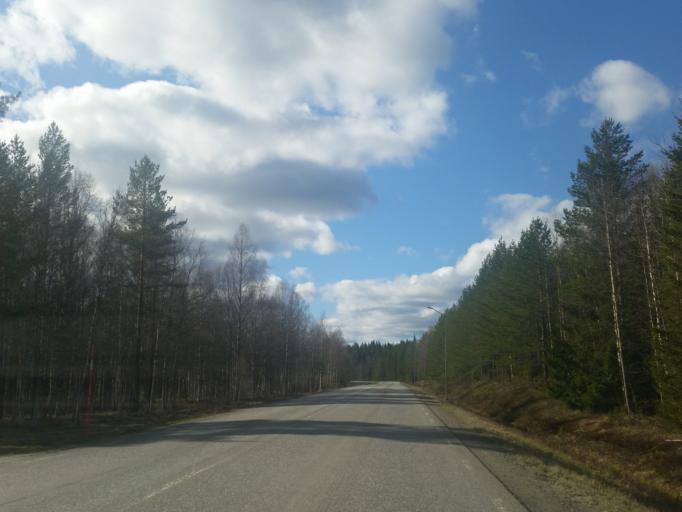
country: SE
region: Vaesterbotten
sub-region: Robertsfors Kommun
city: Robertsfors
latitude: 64.1990
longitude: 20.8343
